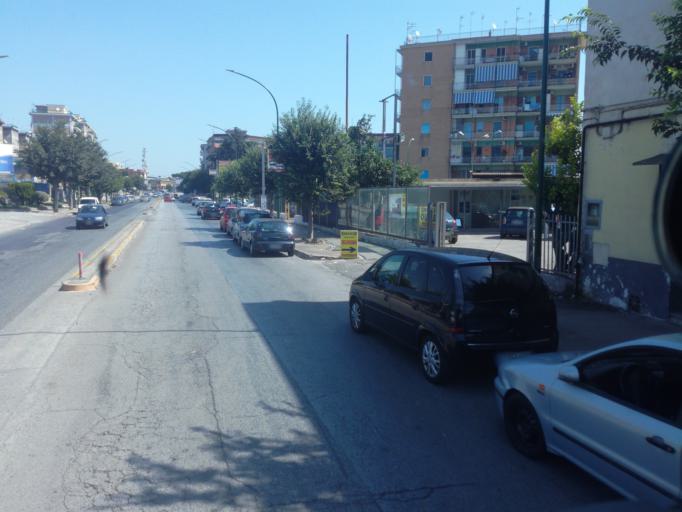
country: IT
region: Campania
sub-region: Provincia di Napoli
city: Arpino
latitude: 40.8869
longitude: 14.3210
